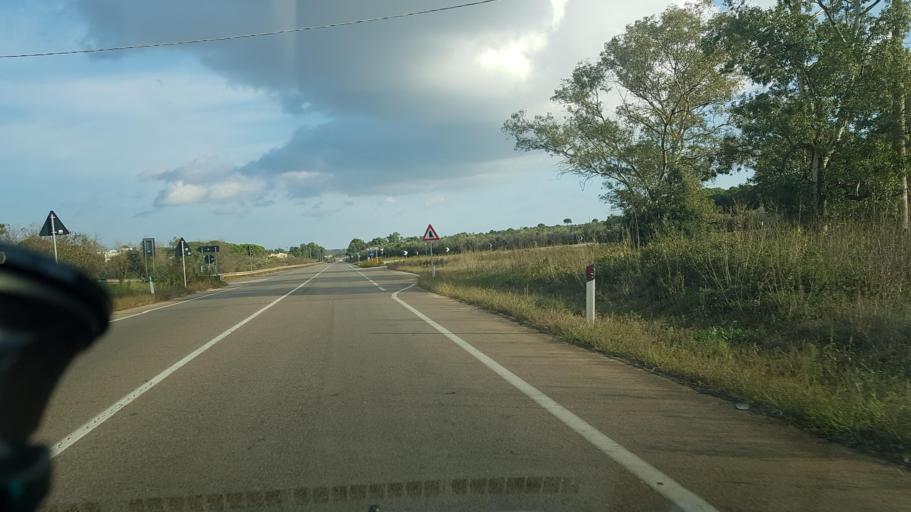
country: IT
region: Apulia
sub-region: Provincia di Lecce
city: Acquarica del Capo
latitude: 39.9007
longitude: 18.2496
